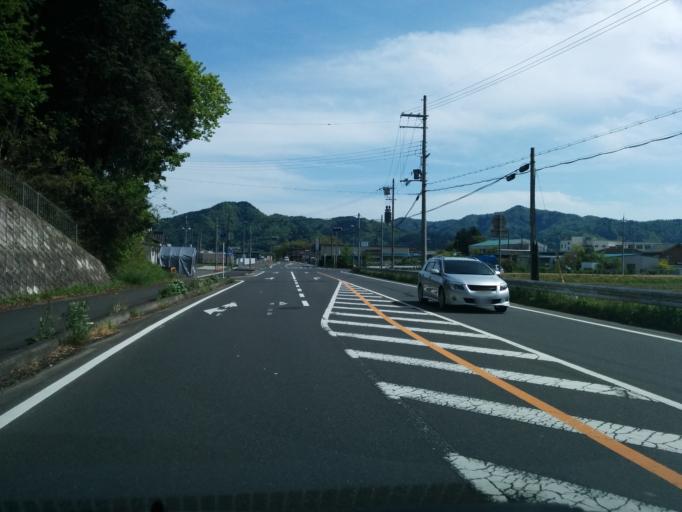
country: JP
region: Kyoto
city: Ayabe
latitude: 35.3234
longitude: 135.2142
